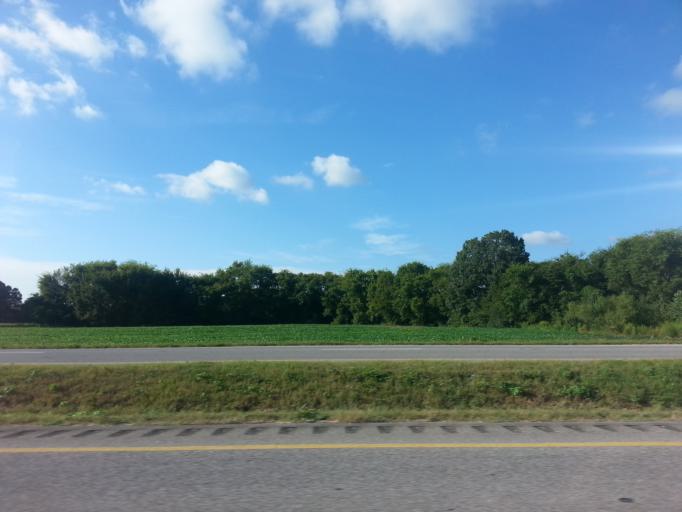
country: US
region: Alabama
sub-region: Colbert County
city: Tuscumbia
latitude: 34.7100
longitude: -87.7329
